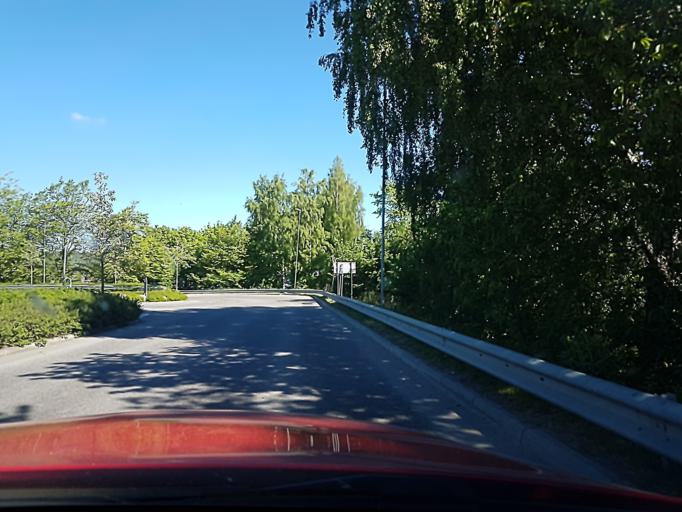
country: SE
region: Vaestra Goetaland
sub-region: Skovde Kommun
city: Skoevde
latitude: 58.4058
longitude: 13.8585
